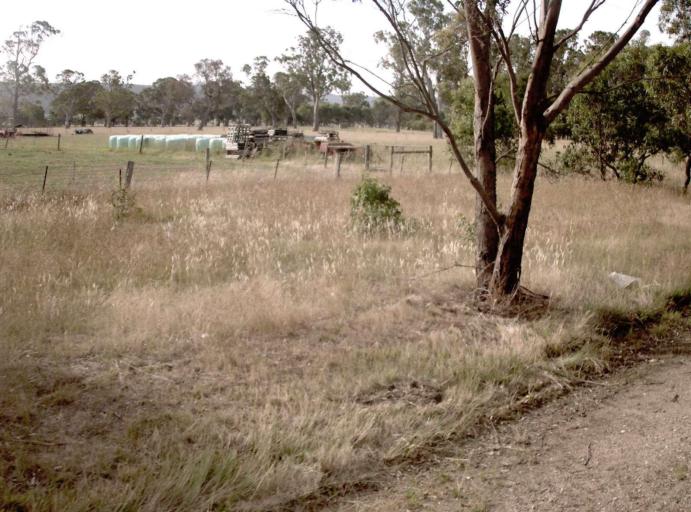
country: AU
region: Victoria
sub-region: Wellington
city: Heyfield
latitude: -38.0324
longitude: 146.6675
